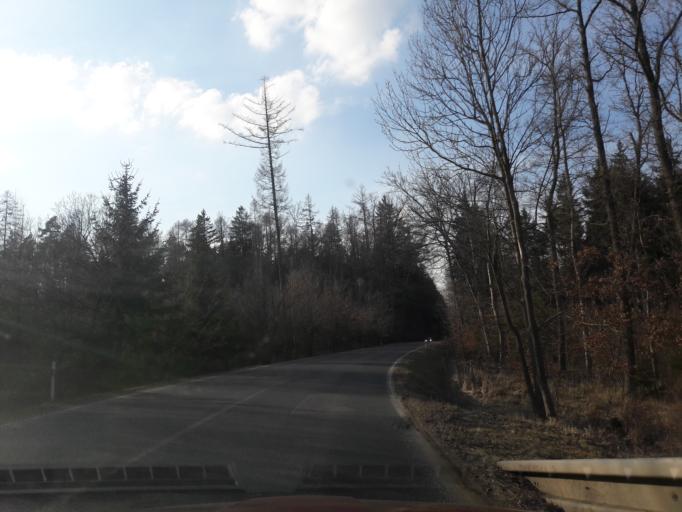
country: CZ
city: Novy Bor
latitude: 50.7490
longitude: 14.5709
